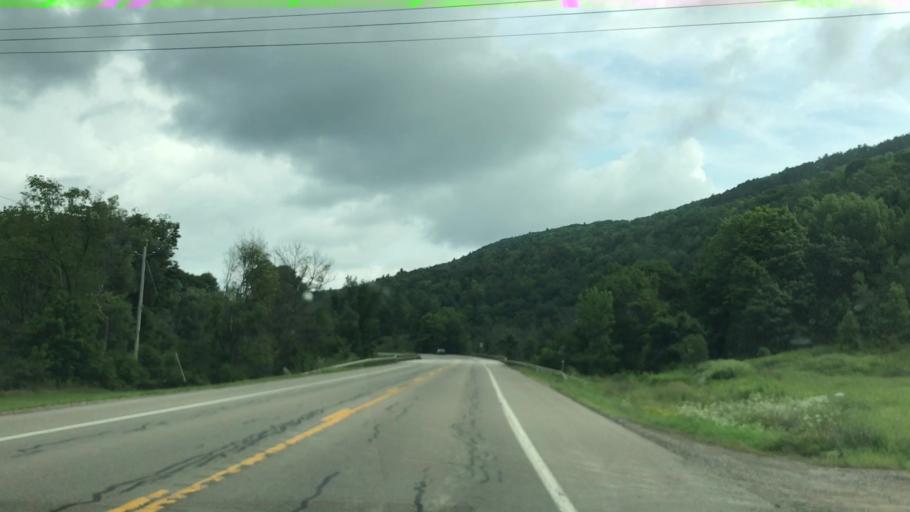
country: US
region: New York
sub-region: Steuben County
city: Bath
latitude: 42.3902
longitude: -77.3509
